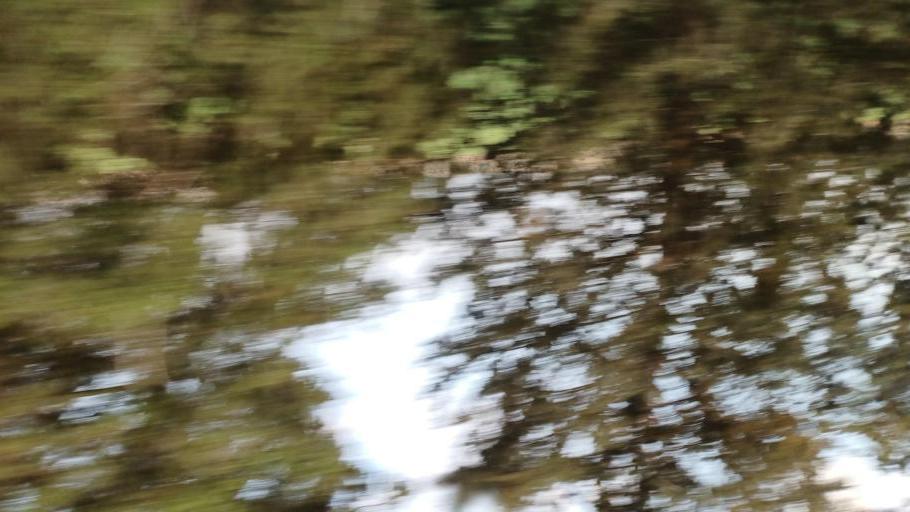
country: CY
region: Lefkosia
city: Lympia
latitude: 35.0179
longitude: 33.4954
